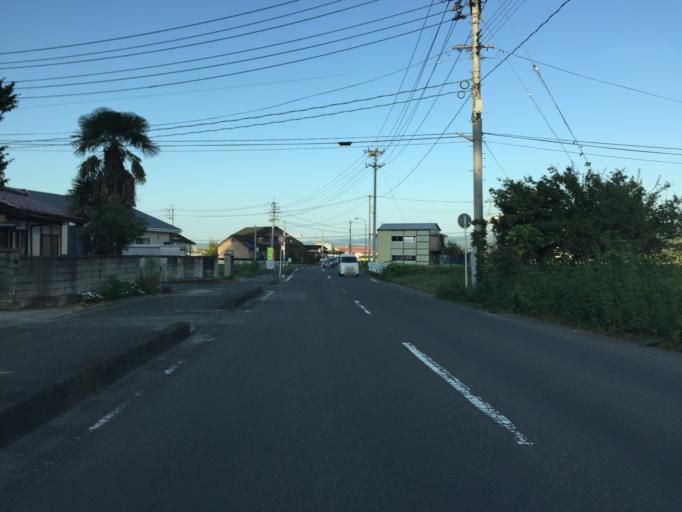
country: JP
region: Fukushima
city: Hobaramachi
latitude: 37.8049
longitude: 140.5505
